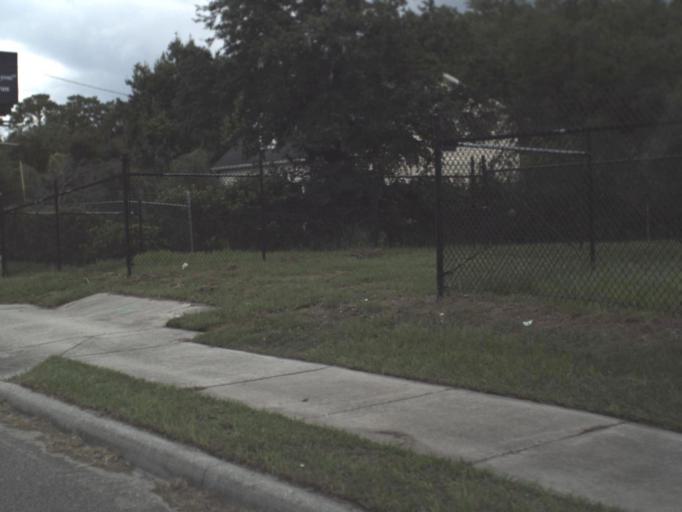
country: US
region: Florida
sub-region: Pasco County
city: Land O' Lakes
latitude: 28.2284
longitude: -82.4578
